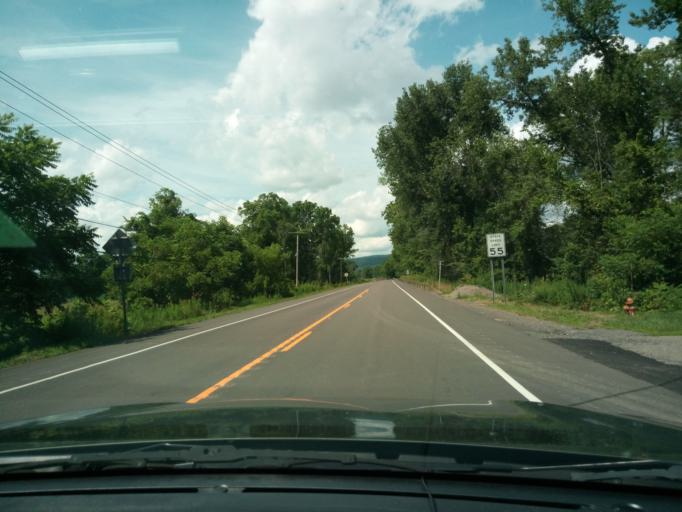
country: US
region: New York
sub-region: Chemung County
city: Southport
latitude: 42.0257
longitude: -76.7415
